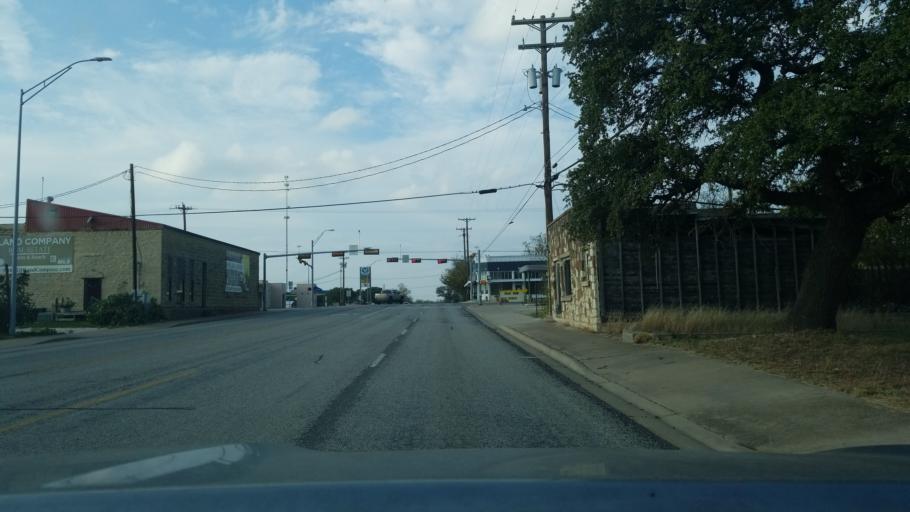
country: US
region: Texas
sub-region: Lampasas County
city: Lampasas
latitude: 31.2158
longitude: -98.3934
